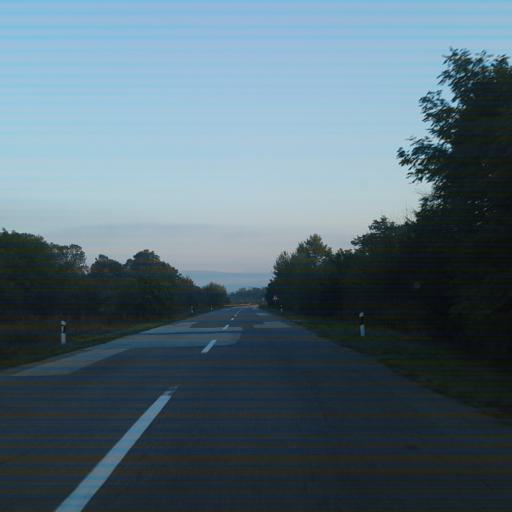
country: RS
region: Central Serbia
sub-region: Zajecarski Okrug
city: Zajecar
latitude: 43.9733
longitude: 22.2924
